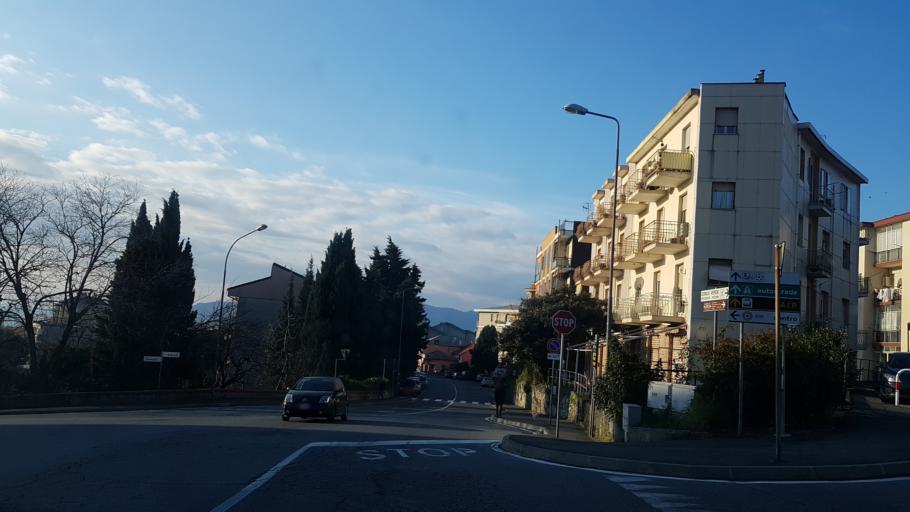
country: IT
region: Liguria
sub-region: Provincia di Savona
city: Savona
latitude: 44.3041
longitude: 8.4601
